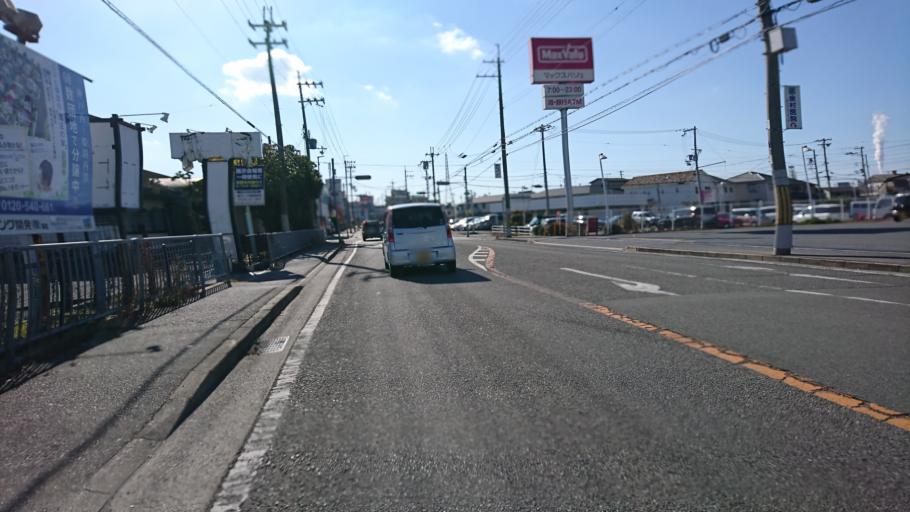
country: JP
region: Hyogo
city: Kakogawacho-honmachi
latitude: 34.7747
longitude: 134.8035
